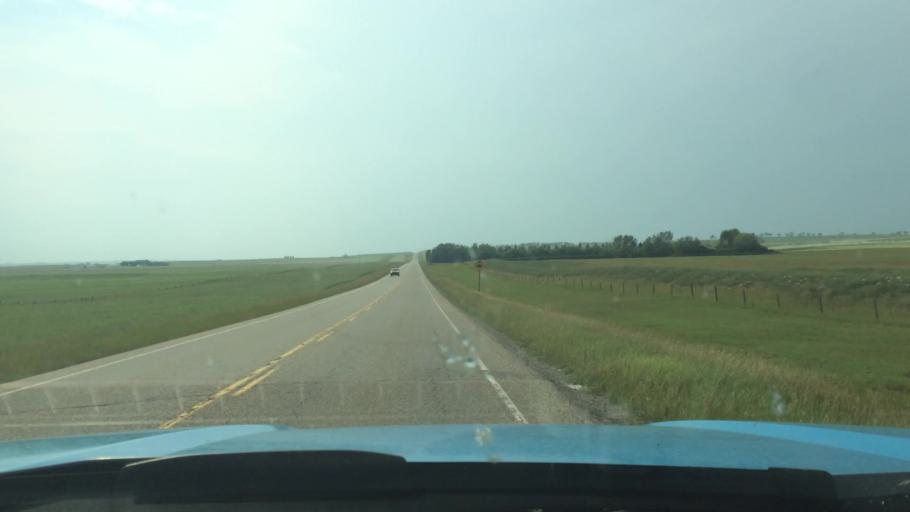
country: CA
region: Alberta
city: Airdrie
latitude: 51.2125
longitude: -114.0825
